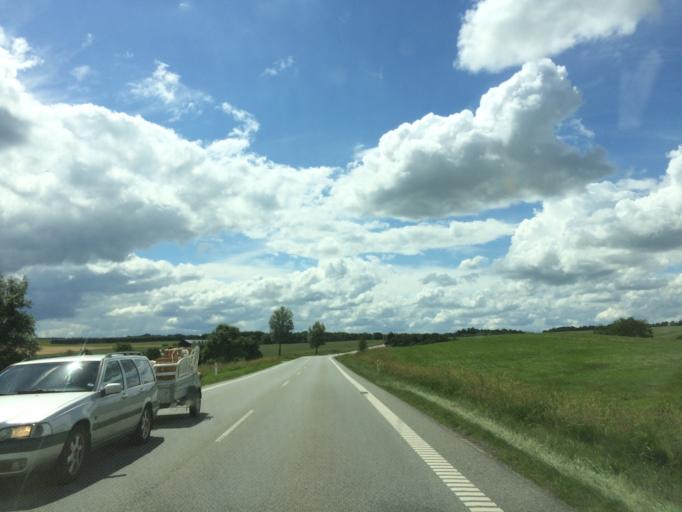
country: DK
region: North Denmark
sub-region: Mariagerfjord Kommune
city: Hobro
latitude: 56.6181
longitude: 9.7167
